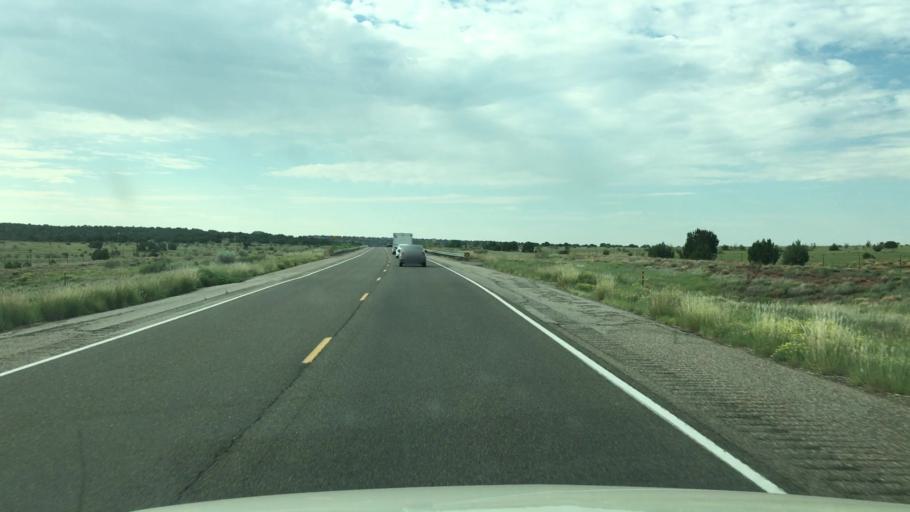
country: US
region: New Mexico
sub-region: Santa Fe County
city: Eldorado at Santa Fe
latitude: 35.2937
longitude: -105.8256
